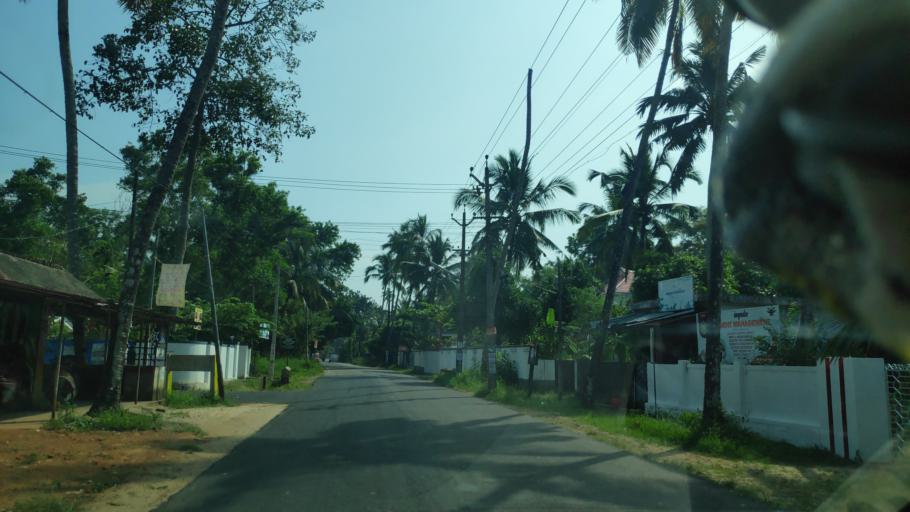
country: IN
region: Kerala
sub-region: Alappuzha
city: Shertallai
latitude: 9.6190
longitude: 76.3005
